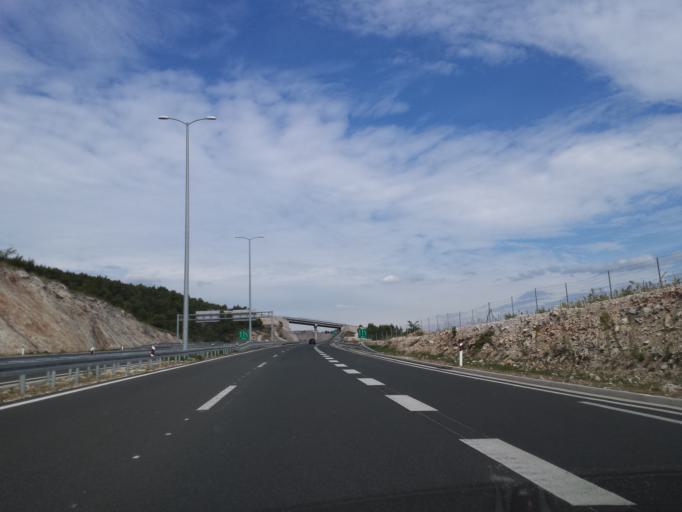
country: BA
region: Federation of Bosnia and Herzegovina
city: Ljubuski
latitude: 43.1529
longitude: 17.4812
